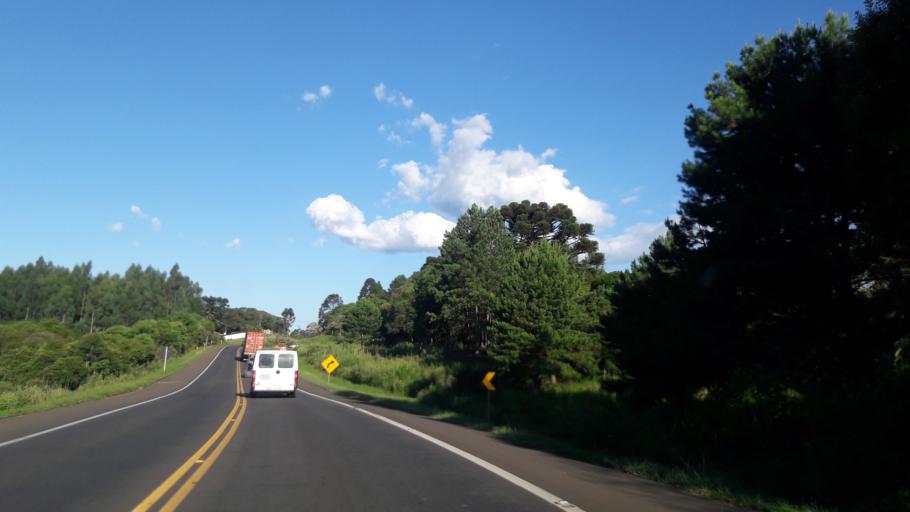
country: BR
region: Parana
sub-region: Guarapuava
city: Guarapuava
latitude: -25.3679
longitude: -51.3389
